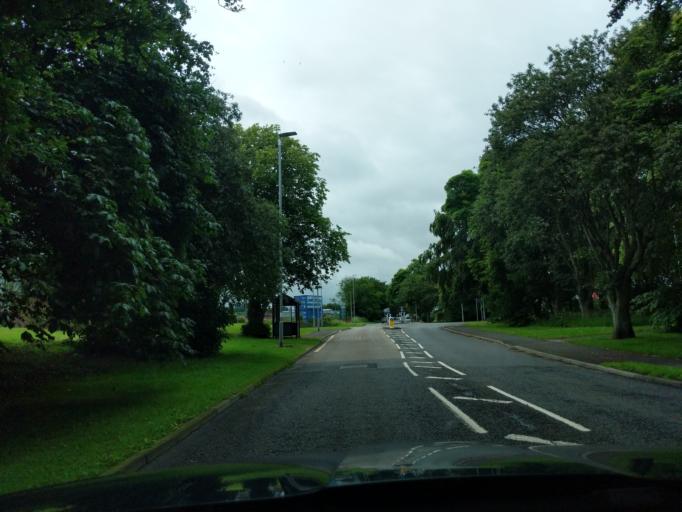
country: GB
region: England
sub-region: Northumberland
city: Berwick-Upon-Tweed
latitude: 55.7641
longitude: -2.0214
